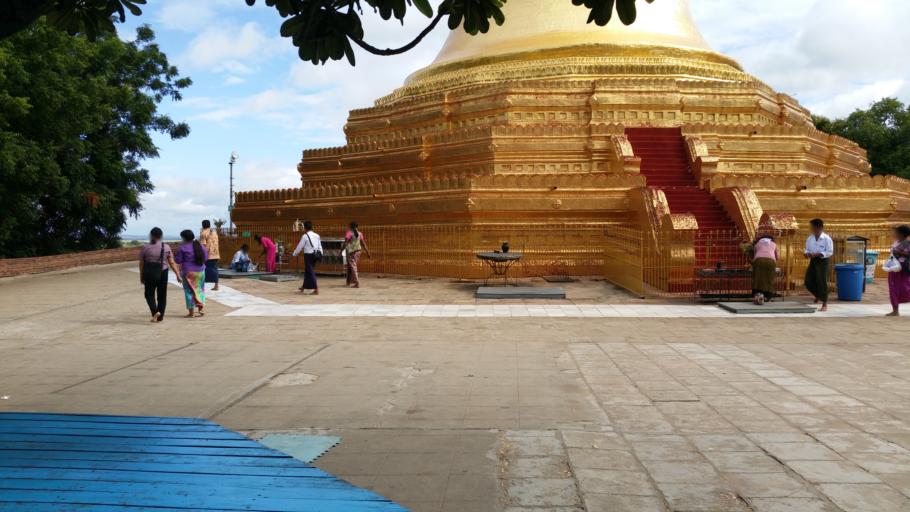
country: MM
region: Magway
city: Chauk
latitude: 21.1270
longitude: 94.8505
